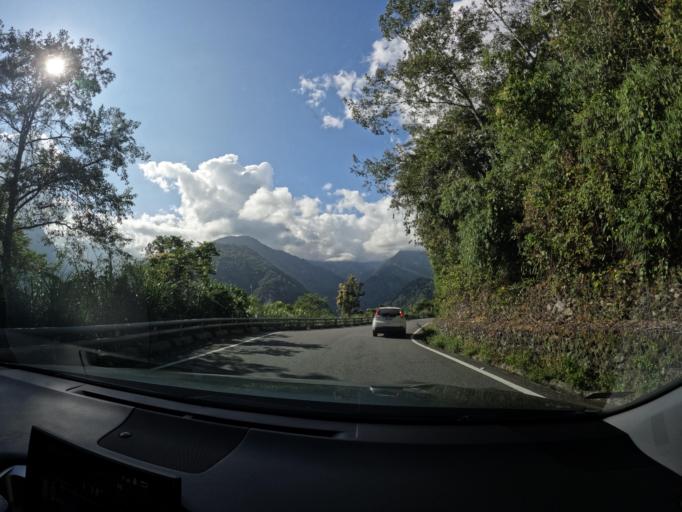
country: TW
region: Taiwan
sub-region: Taitung
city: Taitung
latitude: 23.1953
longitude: 121.0200
